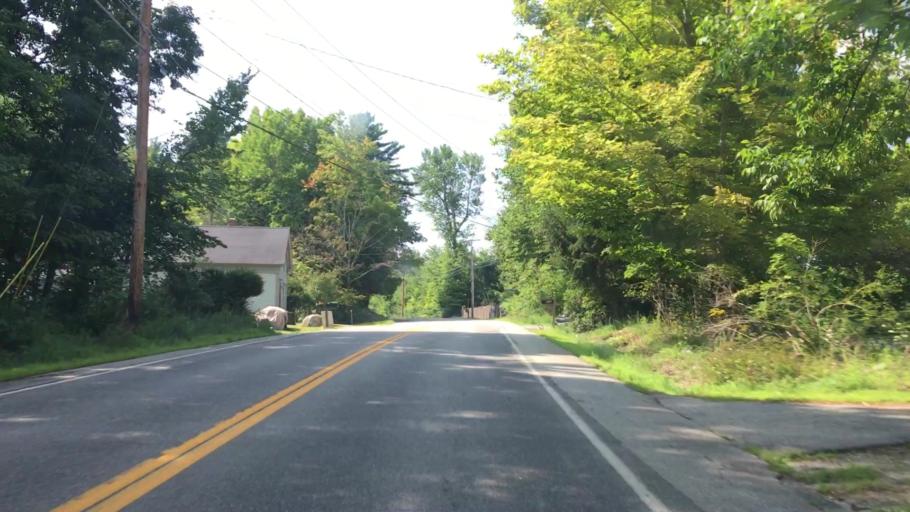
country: US
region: Maine
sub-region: Cumberland County
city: Raymond
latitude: 43.9184
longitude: -70.4370
